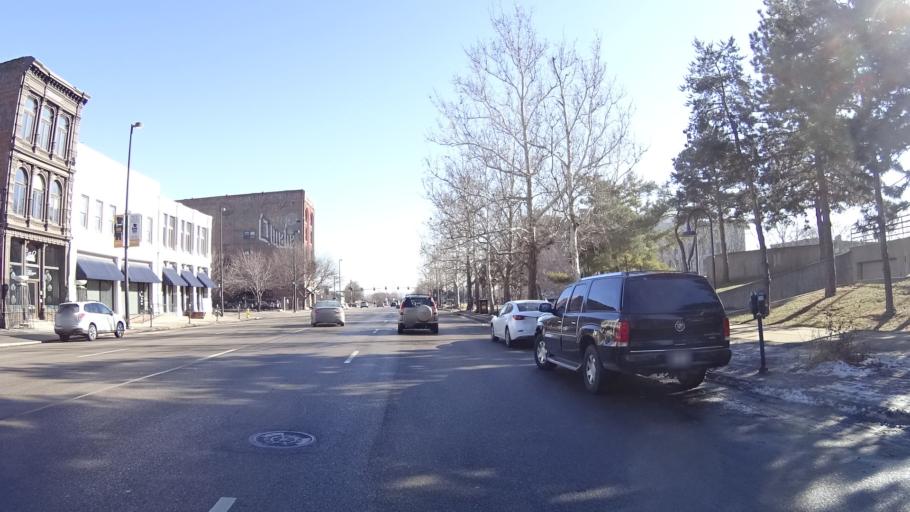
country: US
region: Nebraska
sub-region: Douglas County
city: Omaha
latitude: 41.2586
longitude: -95.9315
